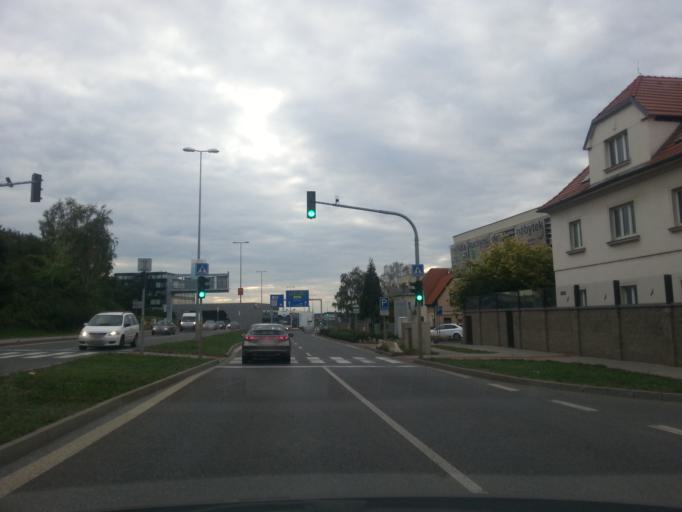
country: CZ
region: Central Bohemia
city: Hostivice
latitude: 50.0770
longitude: 14.3022
